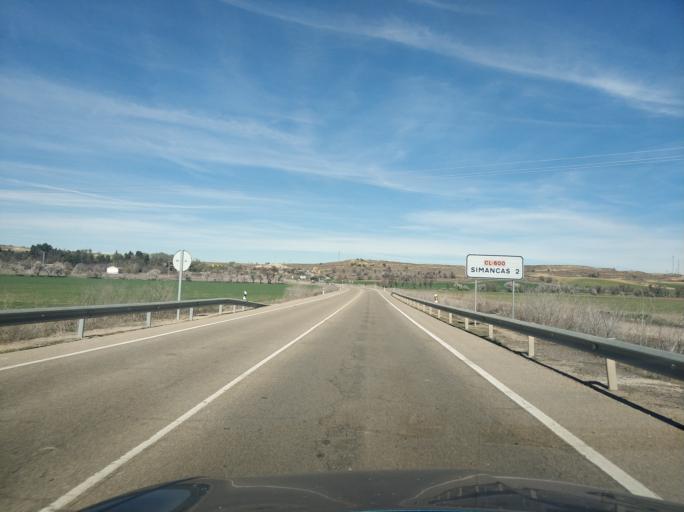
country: ES
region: Castille and Leon
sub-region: Provincia de Valladolid
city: Simancas
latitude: 41.5905
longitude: -4.8181
